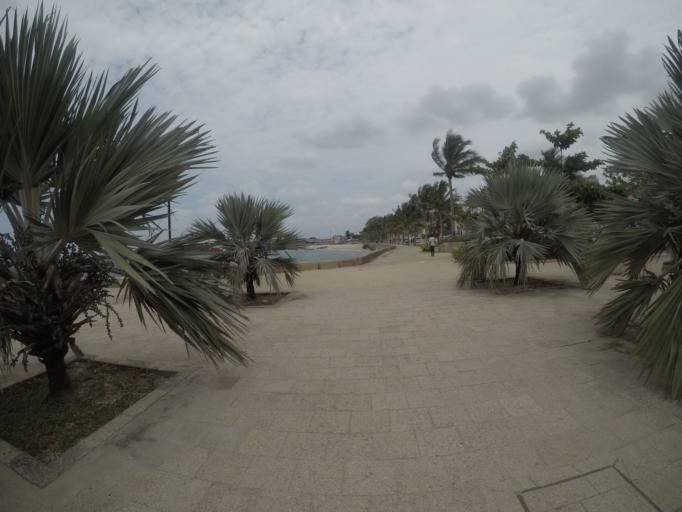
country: TZ
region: Zanzibar Urban/West
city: Zanzibar
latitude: -6.1600
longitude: 39.1895
